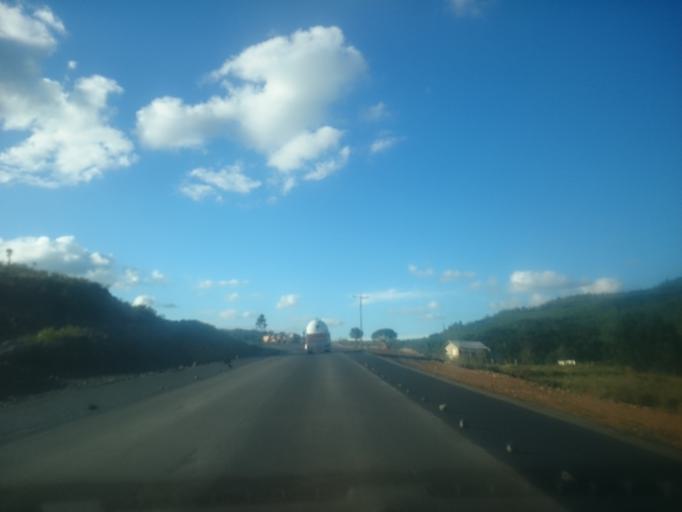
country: BR
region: Santa Catarina
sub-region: Sao Joaquim
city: Sao Joaquim
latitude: -28.0859
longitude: -50.0618
